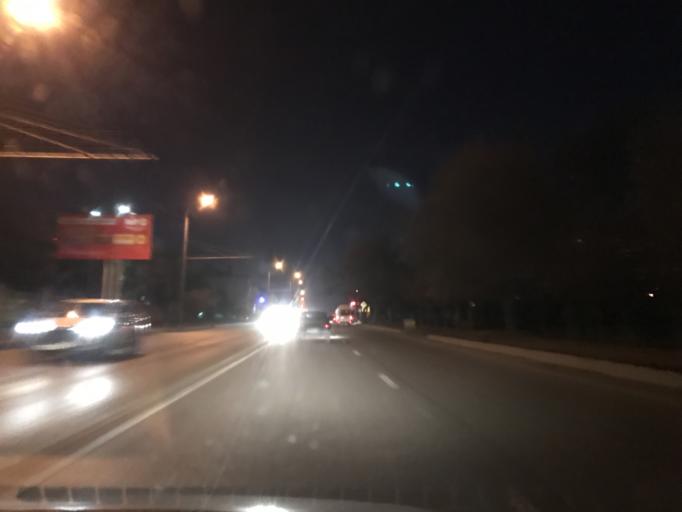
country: RU
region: Rostov
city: Kalinin
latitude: 47.2053
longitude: 39.6136
